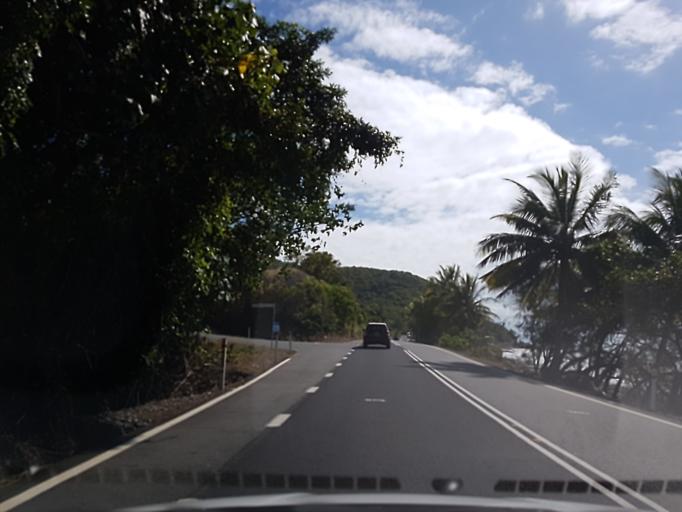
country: AU
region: Queensland
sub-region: Cairns
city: Port Douglas
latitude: -16.5820
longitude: 145.5125
